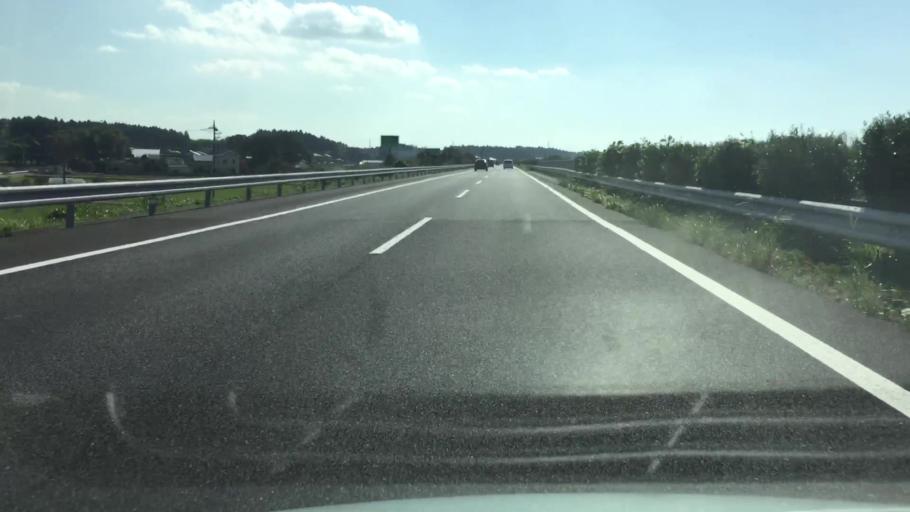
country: JP
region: Ibaraki
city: Tomobe
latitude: 36.3221
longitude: 140.3031
